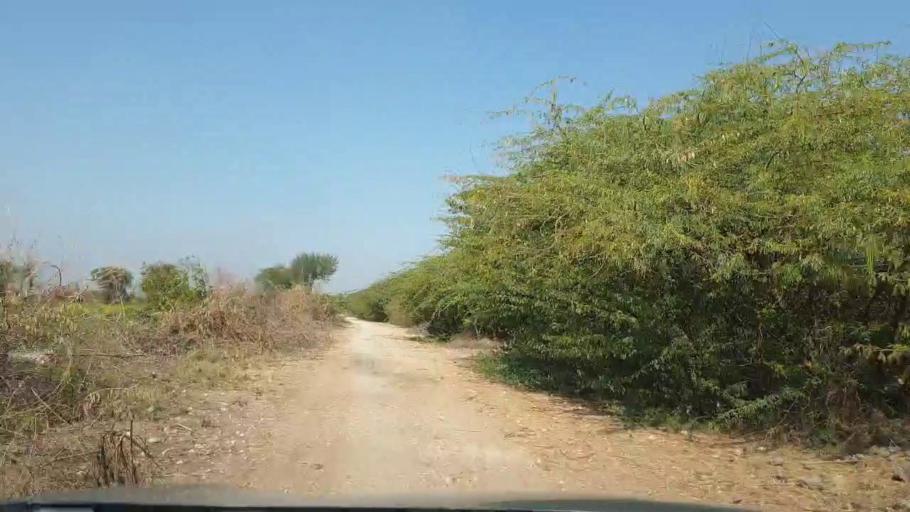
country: PK
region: Sindh
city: Berani
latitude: 25.6817
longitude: 68.8960
